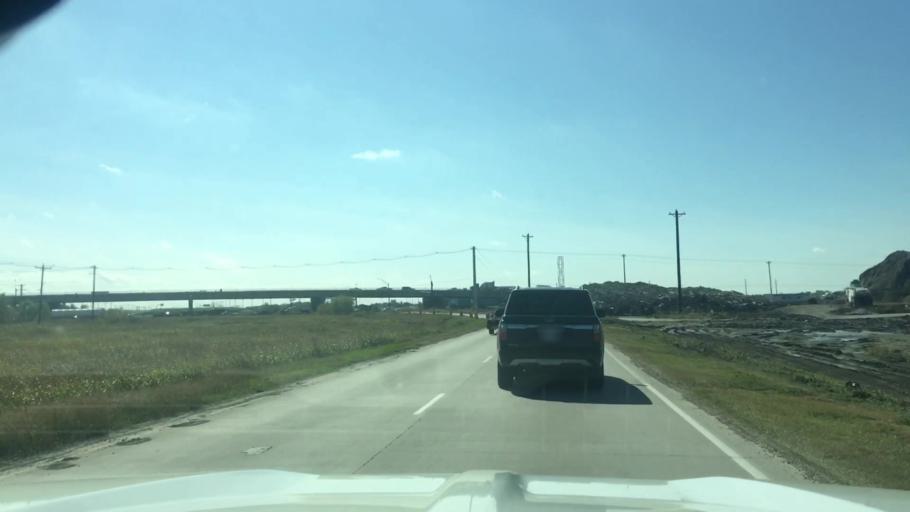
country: US
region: Texas
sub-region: Collin County
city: Prosper
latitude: 33.2217
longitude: -96.8201
